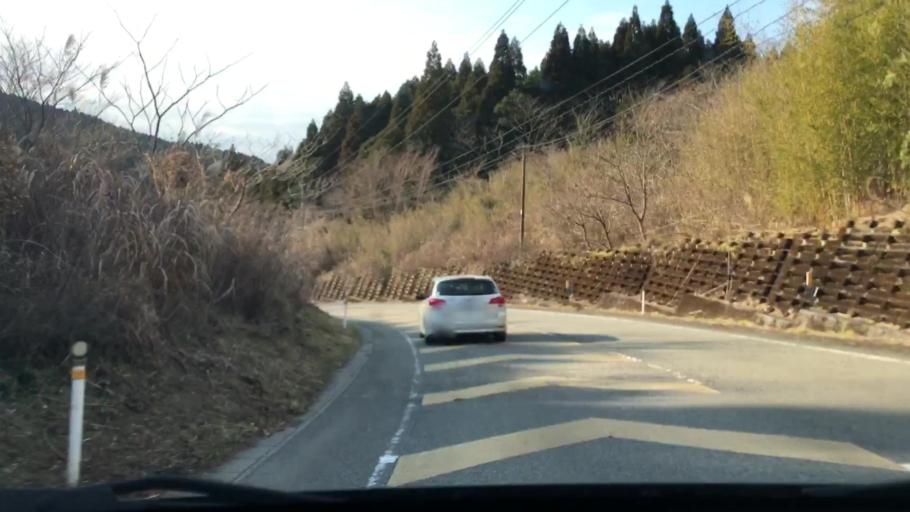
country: JP
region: Miyazaki
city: Miyazaki-shi
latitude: 31.7901
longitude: 131.3194
